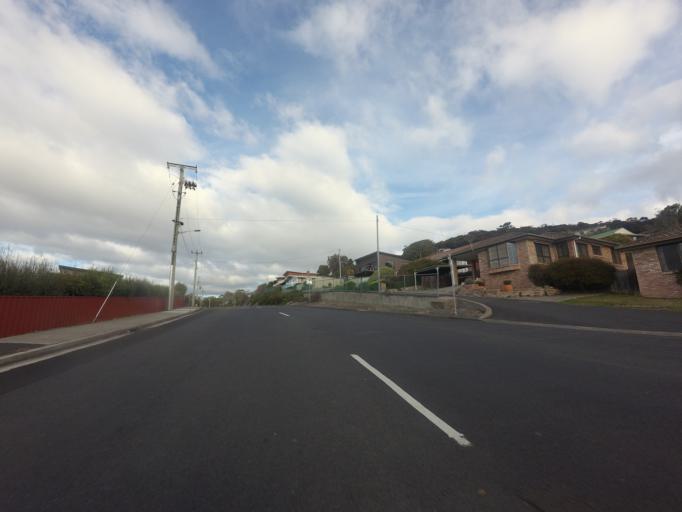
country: AU
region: Tasmania
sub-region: Glenorchy
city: Berriedale
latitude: -42.8167
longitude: 147.2408
